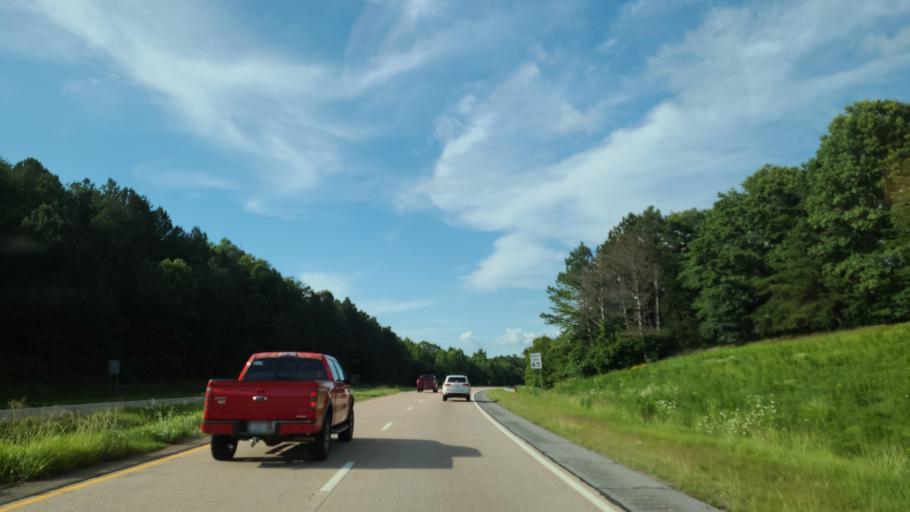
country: US
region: Georgia
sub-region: Gilmer County
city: Ellijay
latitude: 34.5766
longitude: -84.5199
